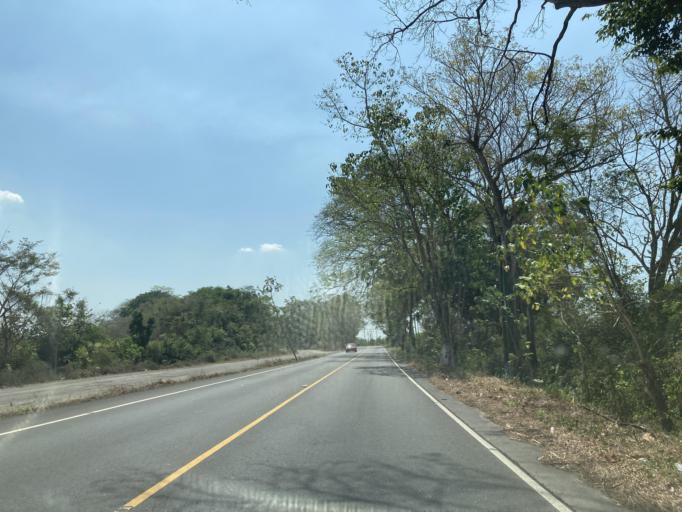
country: GT
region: Escuintla
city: Guanagazapa
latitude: 14.1855
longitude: -90.6921
